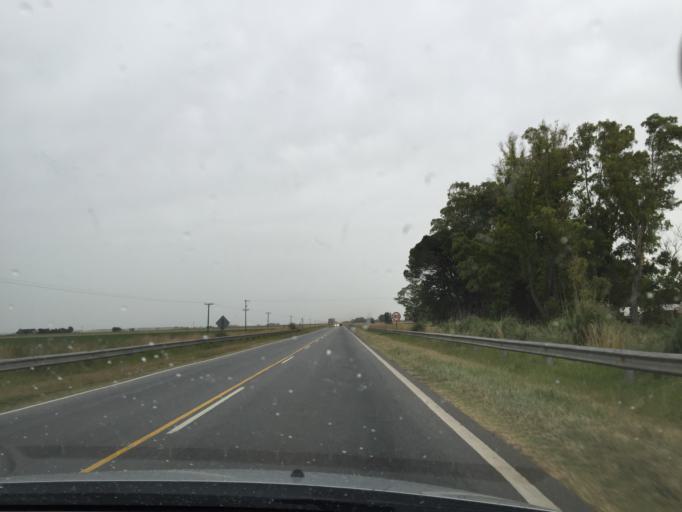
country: AR
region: Buenos Aires
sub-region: Partido de Tandil
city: Tandil
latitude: -37.5570
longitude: -58.7948
